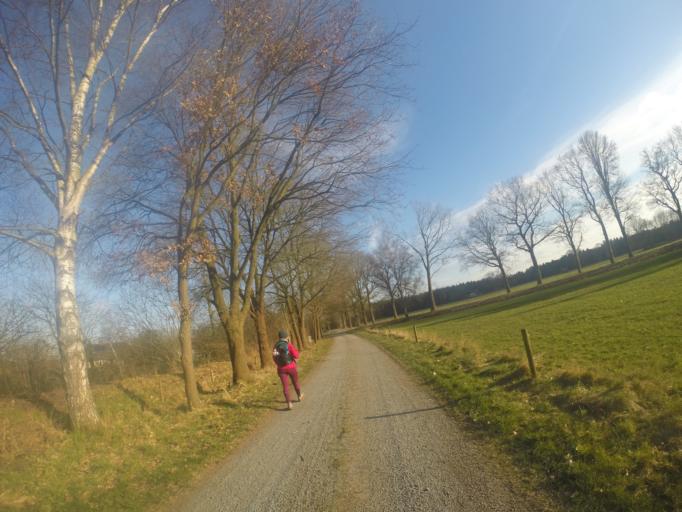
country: NL
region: Gelderland
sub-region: Gemeente Lochem
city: Lochem
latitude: 52.1274
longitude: 6.3588
